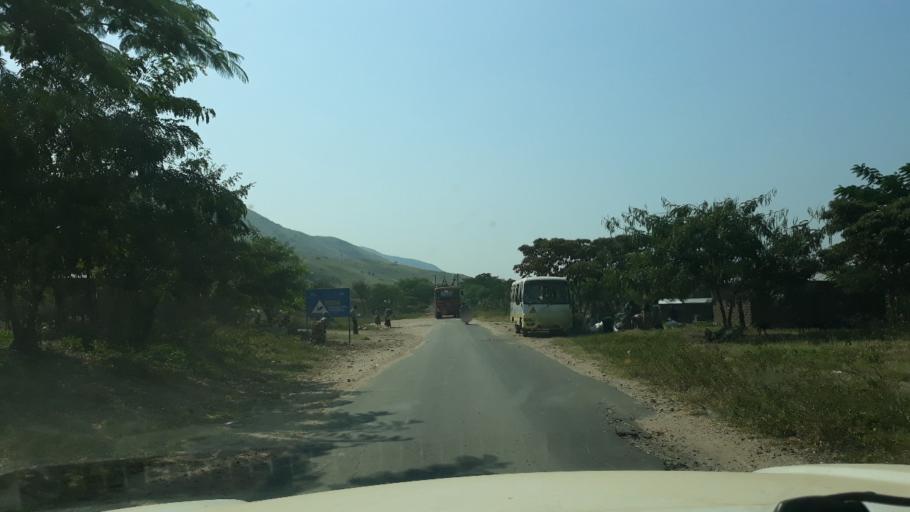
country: CD
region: South Kivu
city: Uvira
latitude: -3.2852
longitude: 29.1607
